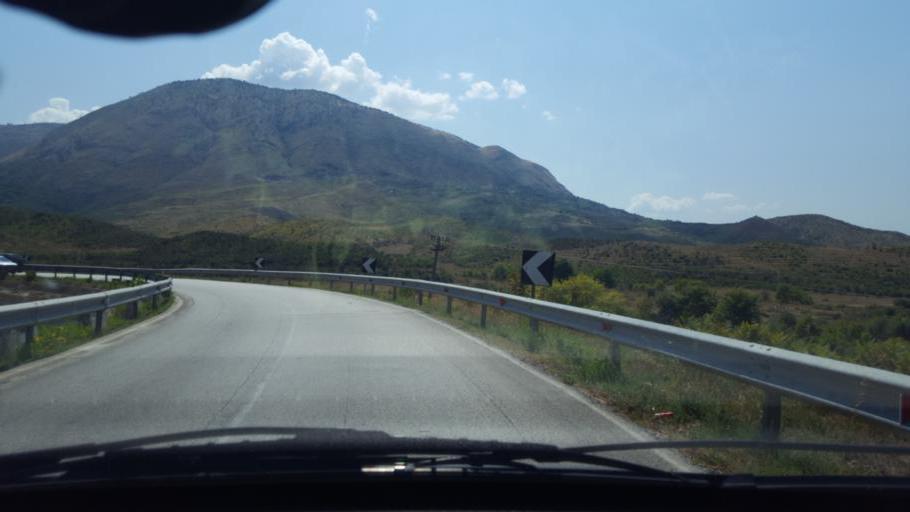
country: AL
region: Vlore
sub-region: Rrethi i Delvines
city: Mesopotam
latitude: 39.9087
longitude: 20.1234
